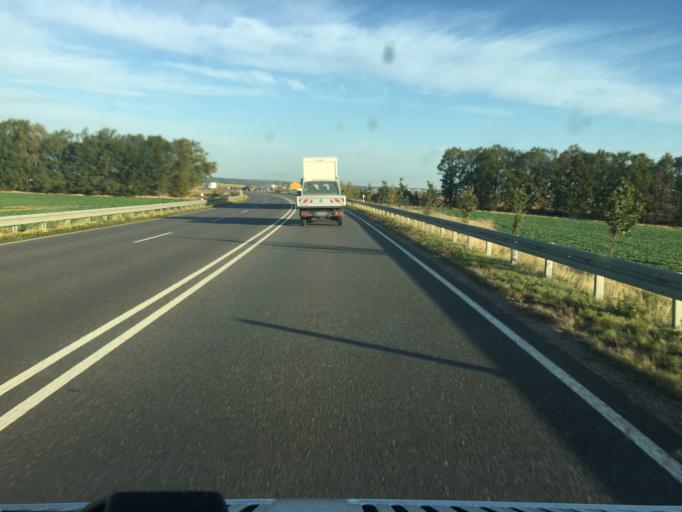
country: DE
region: Saxony
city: Lichtentanne
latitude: 50.6803
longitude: 12.4477
